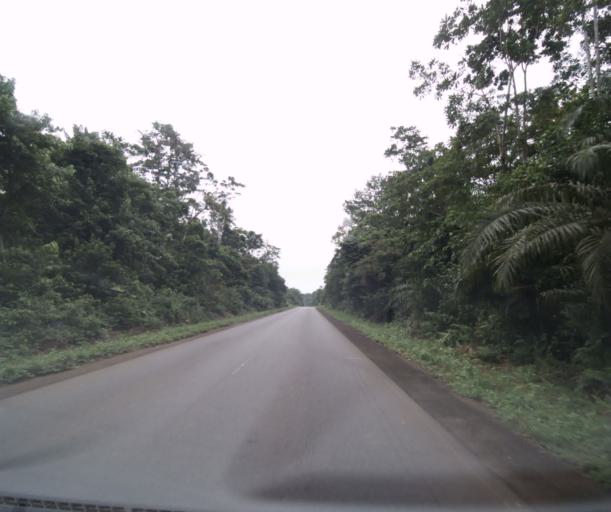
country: CM
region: Littoral
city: Edea
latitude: 3.6742
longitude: 10.1101
